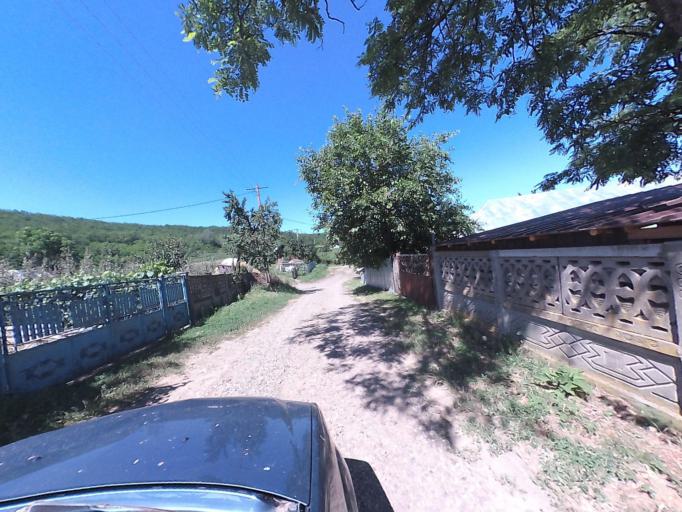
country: RO
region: Vaslui
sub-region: Comuna Costesti
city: Costesti
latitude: 46.4920
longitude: 27.7622
